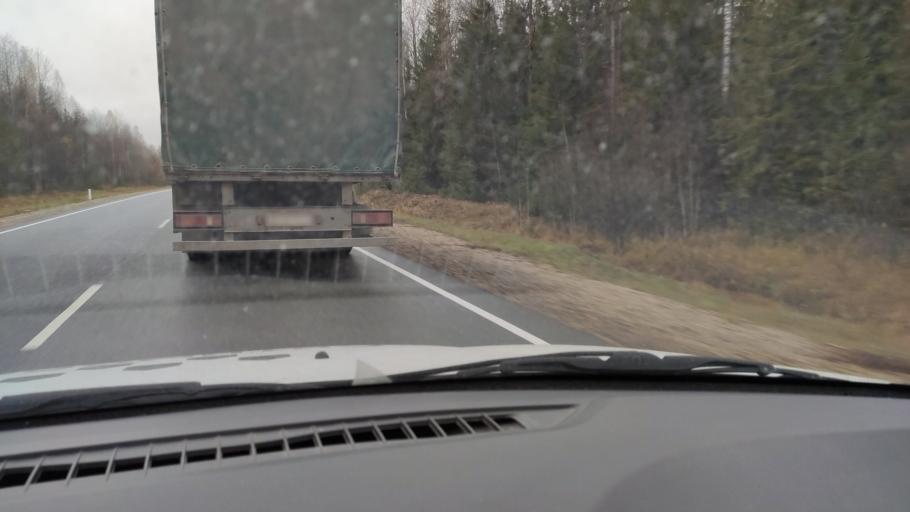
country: RU
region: Kirov
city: Chernaya Kholunitsa
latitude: 58.8013
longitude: 51.8603
